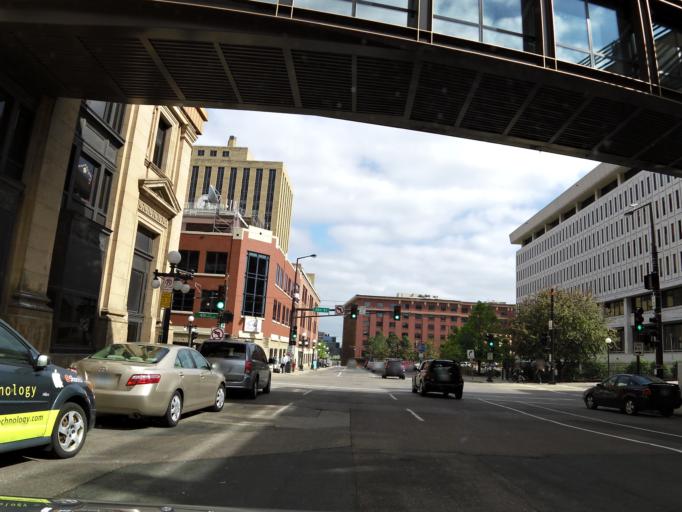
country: US
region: Minnesota
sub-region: Ramsey County
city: Saint Paul
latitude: 44.9474
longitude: -93.0890
